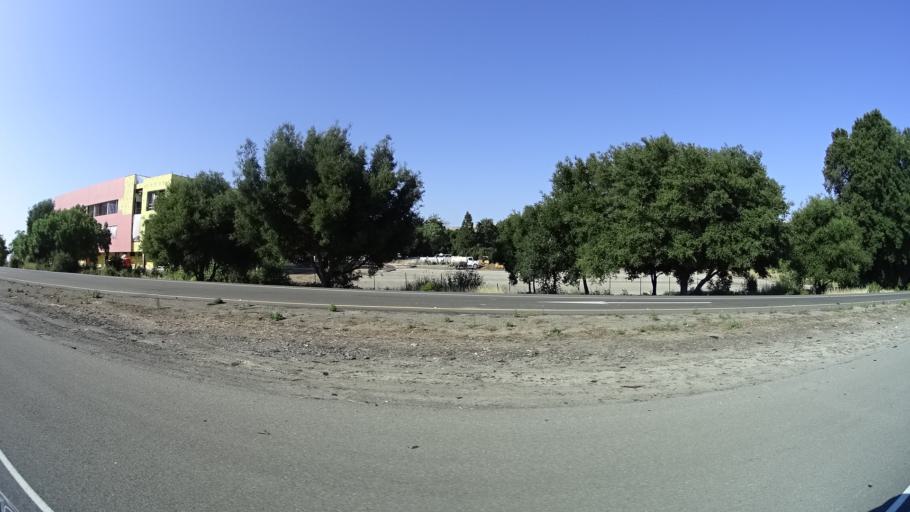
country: US
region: California
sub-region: Santa Clara County
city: Seven Trees
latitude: 37.2539
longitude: -121.7902
